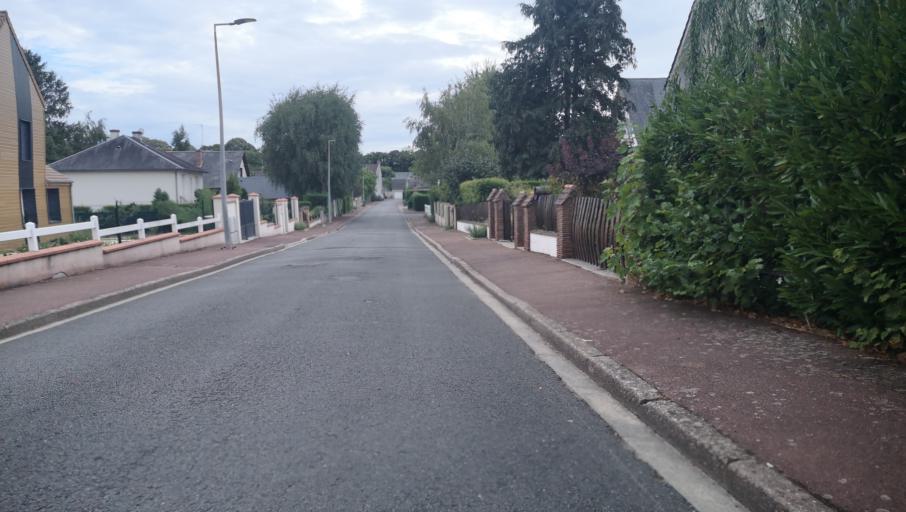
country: FR
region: Centre
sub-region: Departement du Loiret
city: Saint-Jean-de-Braye
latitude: 47.9007
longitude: 1.9906
